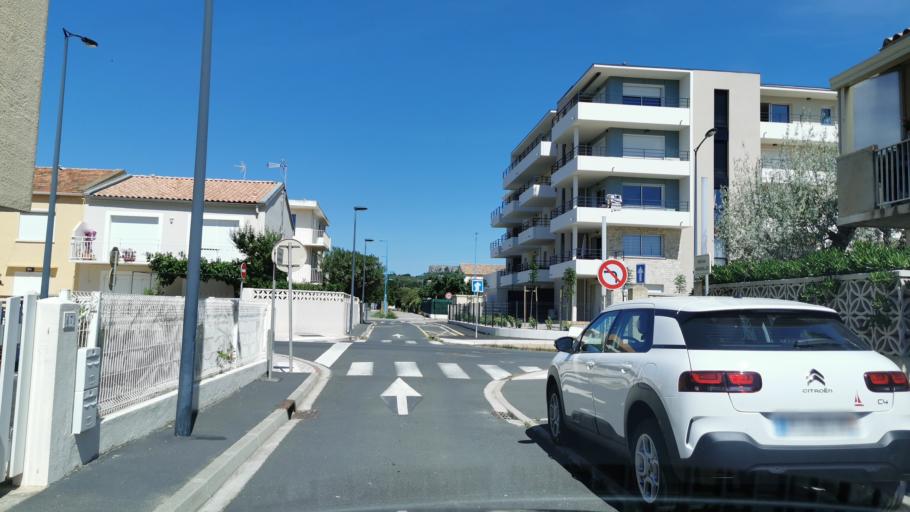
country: FR
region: Languedoc-Roussillon
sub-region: Departement de l'Aude
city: Armissan
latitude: 43.1574
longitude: 3.1637
